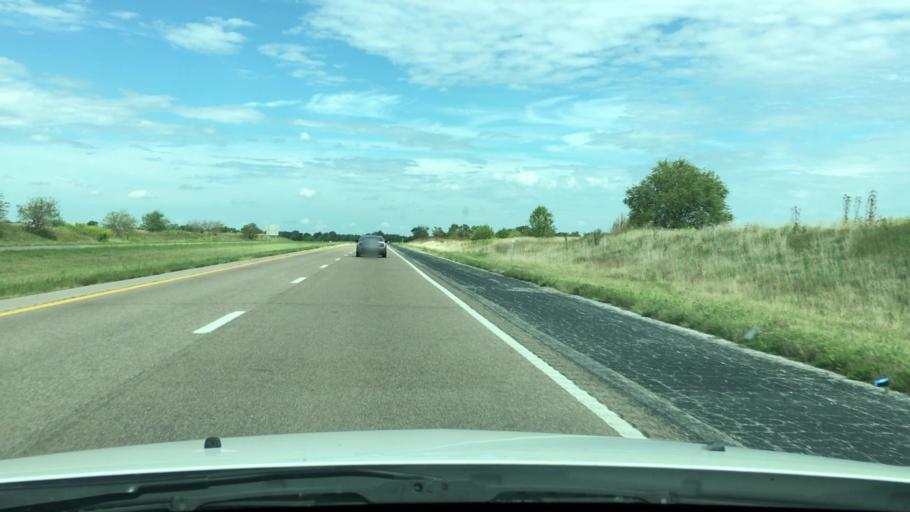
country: US
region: Missouri
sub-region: Audrain County
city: Mexico
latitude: 39.0322
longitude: -91.8874
